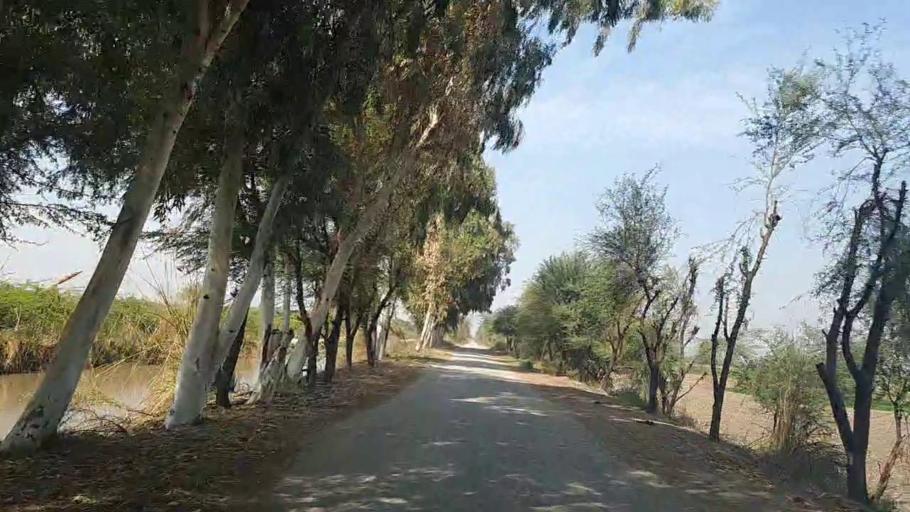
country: PK
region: Sindh
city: Mirpur Khas
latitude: 25.4876
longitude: 68.9237
